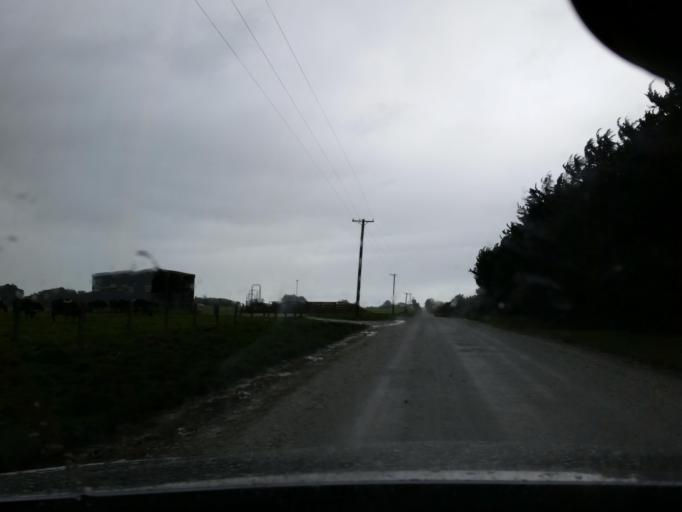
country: NZ
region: Southland
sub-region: Invercargill City
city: Invercargill
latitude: -46.4322
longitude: 168.5062
